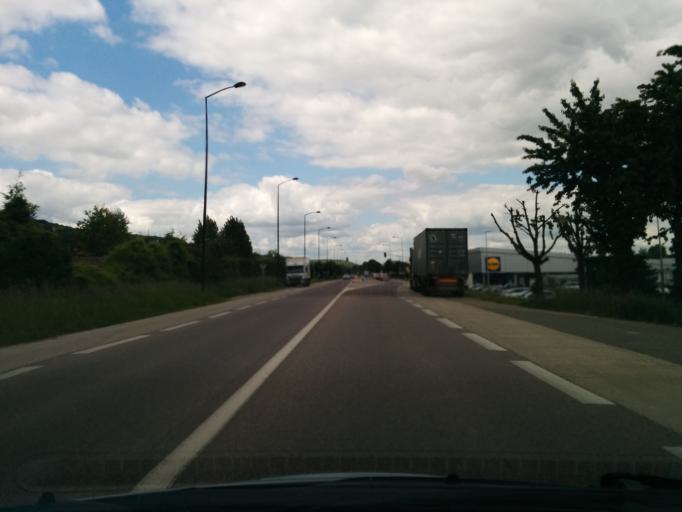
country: FR
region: Ile-de-France
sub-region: Departement des Yvelines
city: Mezieres-sur-Seine
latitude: 48.9615
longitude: 1.8036
